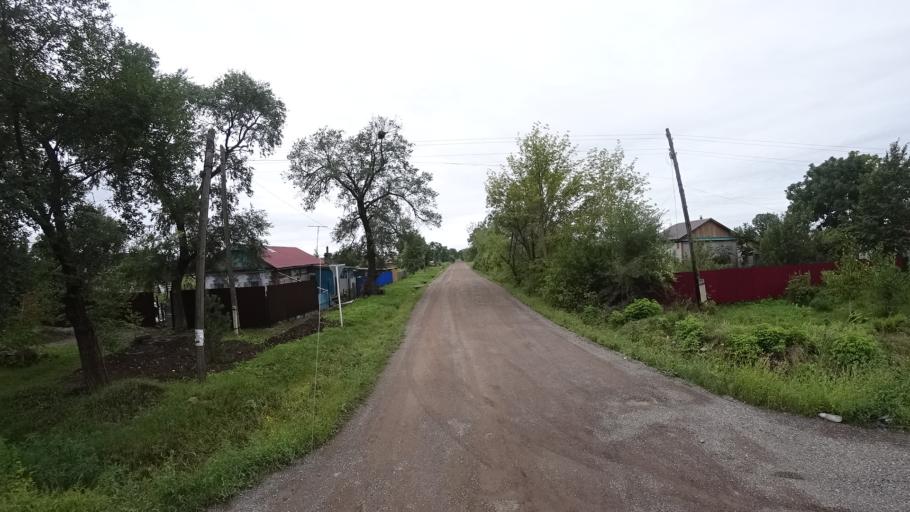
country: RU
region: Primorskiy
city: Chernigovka
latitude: 44.3415
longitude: 132.5693
